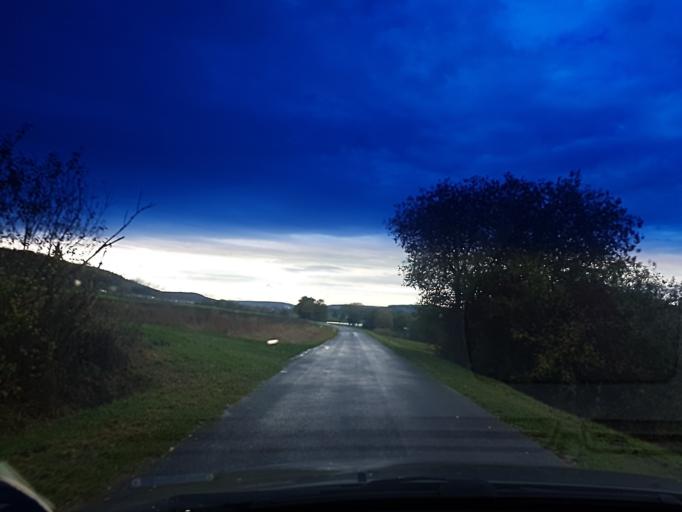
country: DE
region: Bavaria
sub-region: Regierungsbezirk Mittelfranken
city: Burghaslach
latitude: 49.7623
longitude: 10.5624
